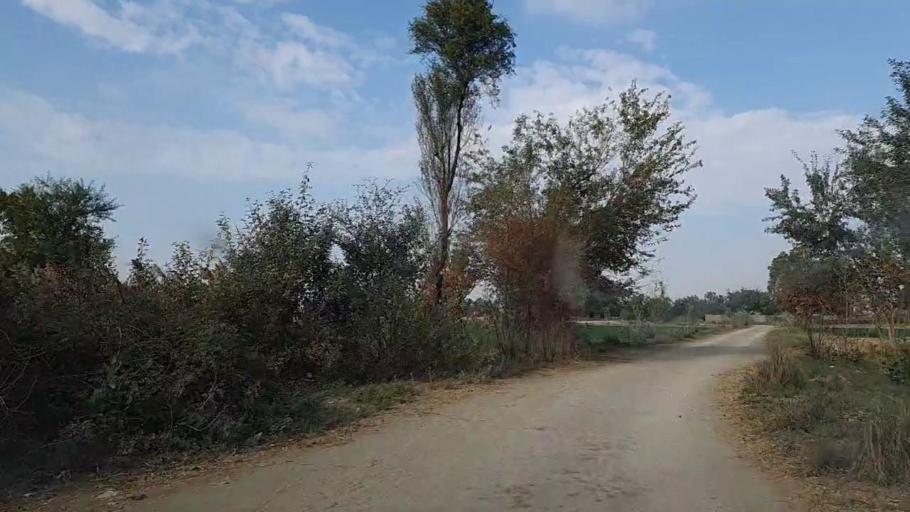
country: PK
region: Sindh
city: Sanghar
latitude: 26.2445
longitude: 69.0168
